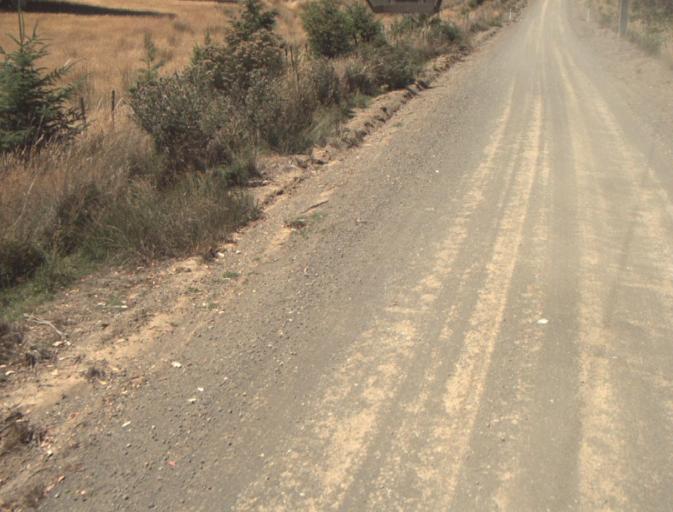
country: AU
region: Tasmania
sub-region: Launceston
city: Newstead
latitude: -41.3441
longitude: 147.3691
